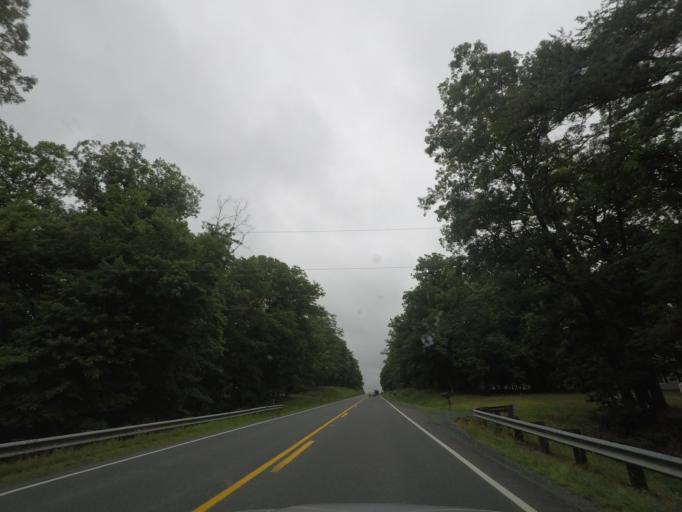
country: US
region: Virginia
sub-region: Fluvanna County
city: Palmyra
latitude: 37.8247
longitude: -78.2701
